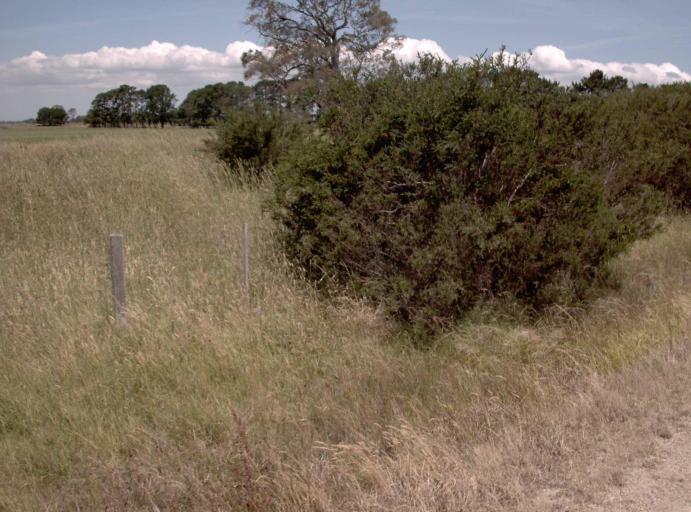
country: AU
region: Victoria
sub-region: Wellington
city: Heyfield
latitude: -38.0335
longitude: 146.8786
